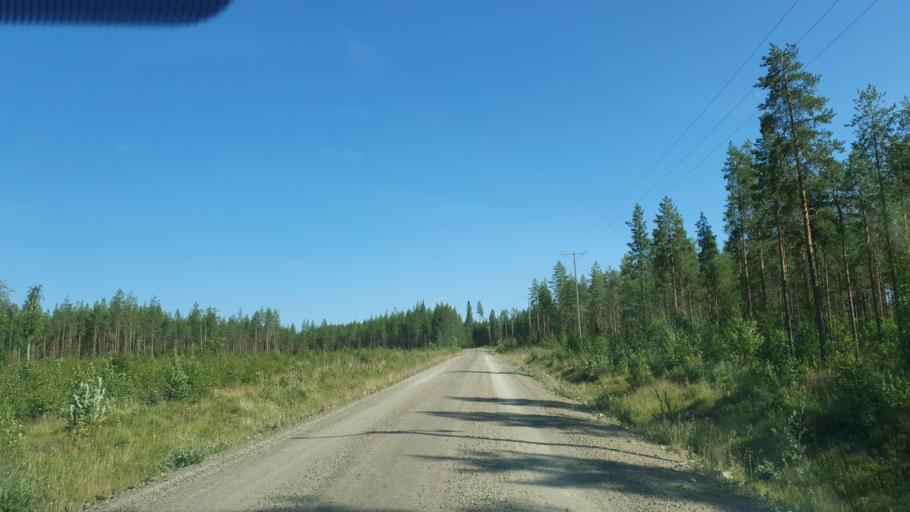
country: FI
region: Kainuu
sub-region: Kehys-Kainuu
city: Kuhmo
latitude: 64.0510
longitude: 29.6022
